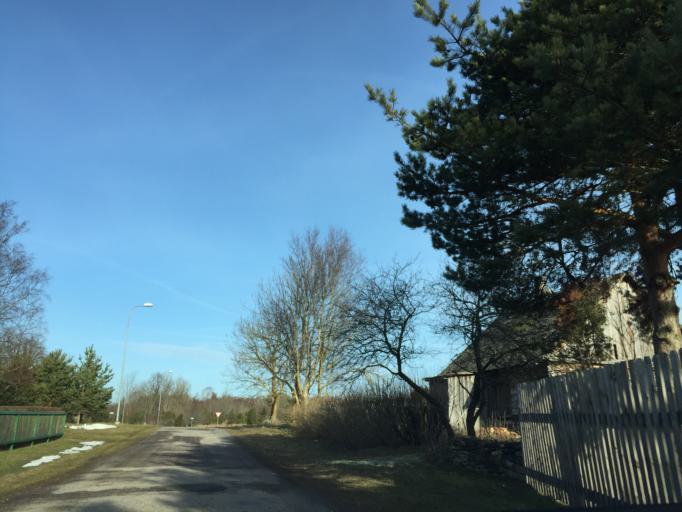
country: EE
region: Saare
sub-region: Kuressaare linn
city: Kuressaare
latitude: 58.3625
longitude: 22.0359
